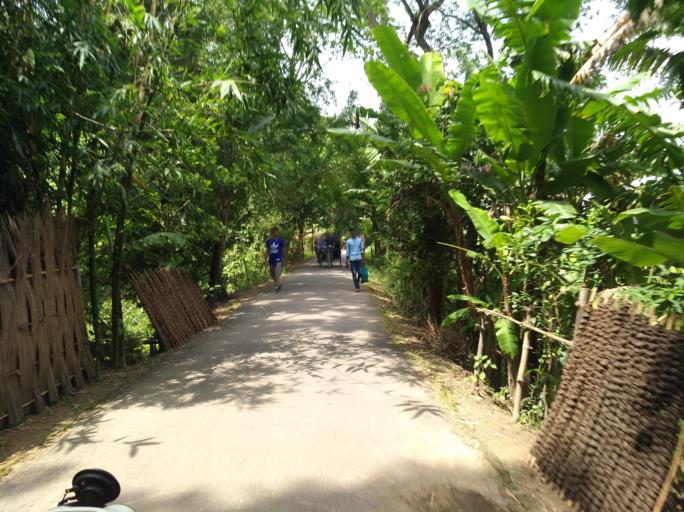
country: BD
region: Dhaka
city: Palang
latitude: 23.2508
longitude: 90.3101
